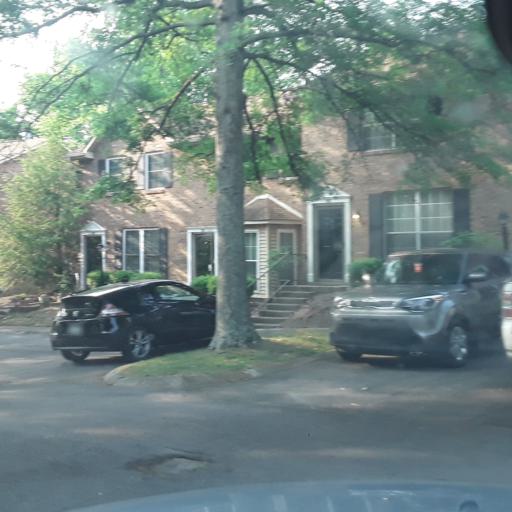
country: US
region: Tennessee
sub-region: Williamson County
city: Brentwood
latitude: 36.0607
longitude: -86.7187
